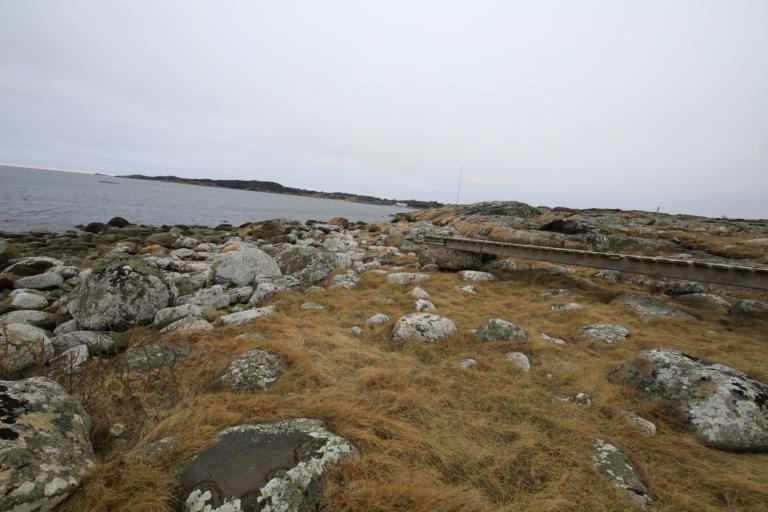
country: SE
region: Halland
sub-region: Kungsbacka Kommun
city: Frillesas
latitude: 57.2461
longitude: 12.1195
